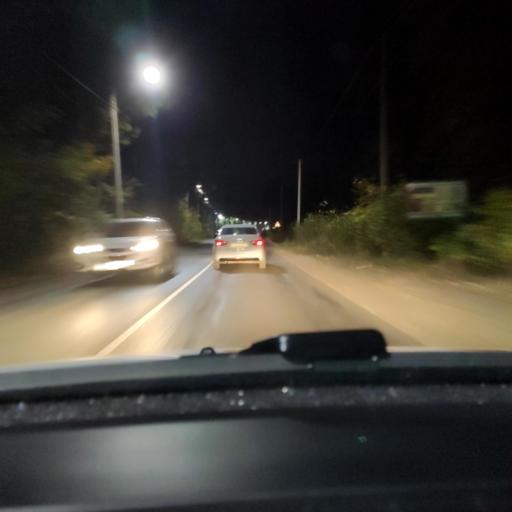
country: RU
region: Voronezj
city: Podgornoye
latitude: 51.7850
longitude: 39.1836
